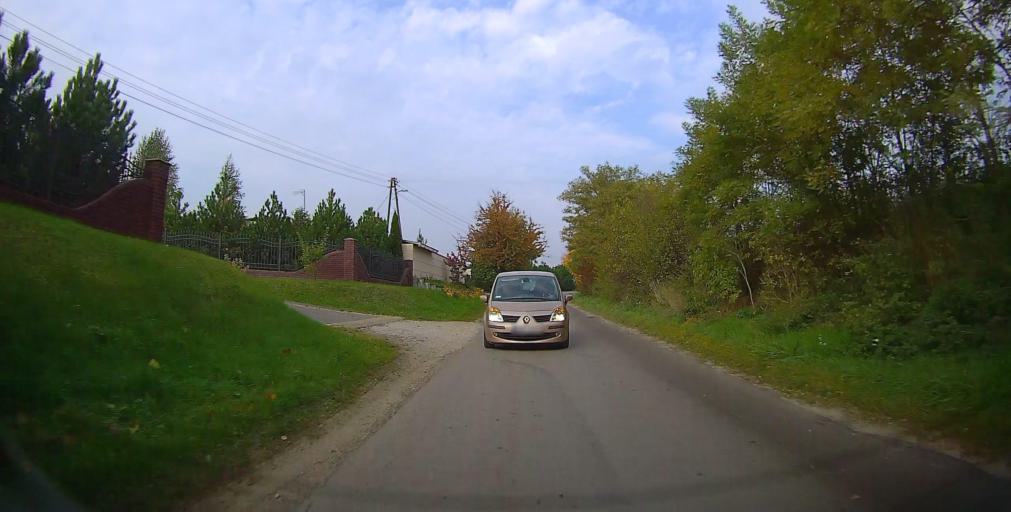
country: PL
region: Masovian Voivodeship
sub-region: Powiat grojecki
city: Mogielnica
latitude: 51.6453
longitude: 20.7359
